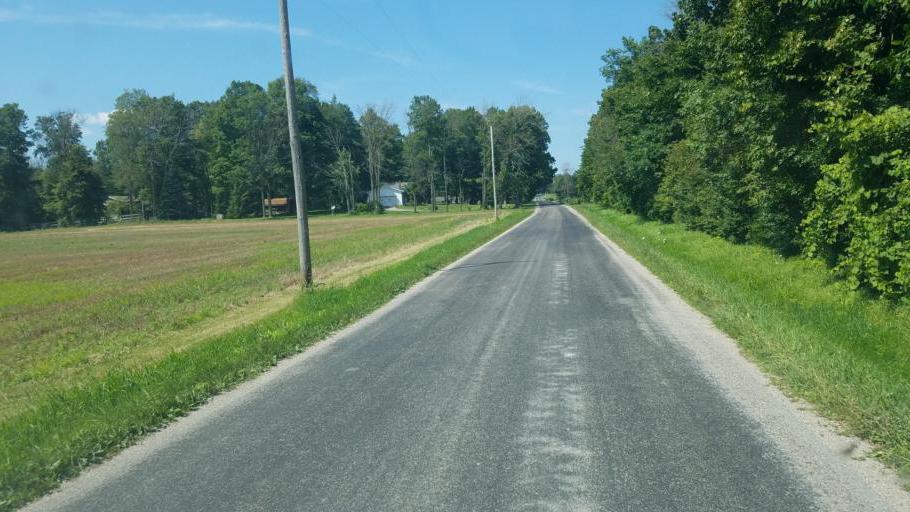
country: US
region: Ohio
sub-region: Crawford County
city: Crestline
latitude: 40.7391
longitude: -82.7219
